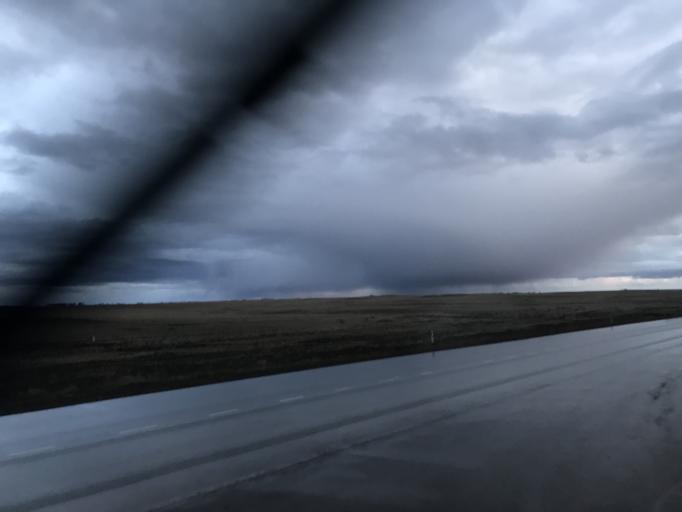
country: KZ
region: Qostanay
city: Ordzhonikidze
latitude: 52.4472
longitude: 61.7726
